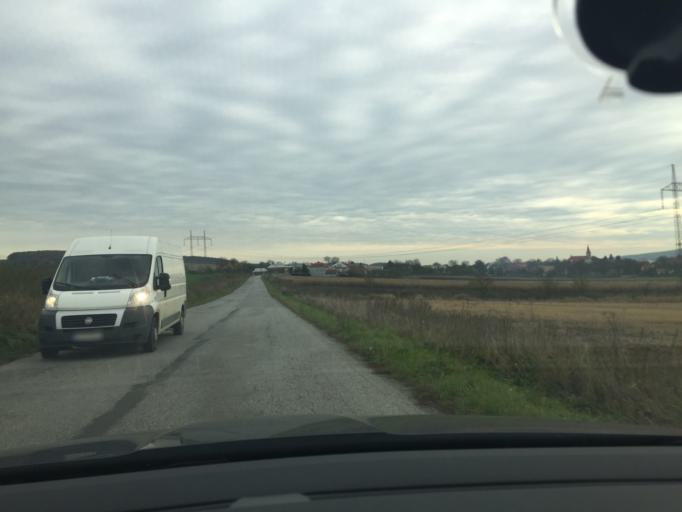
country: SK
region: Kosicky
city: Kosice
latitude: 48.8226
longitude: 21.3225
